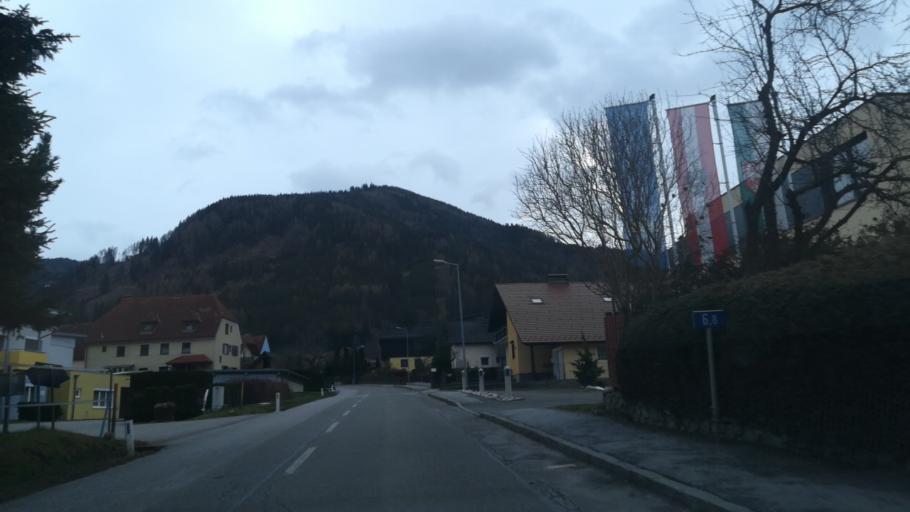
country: AT
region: Styria
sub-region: Politischer Bezirk Murtal
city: Sankt Georgen ob Judenburg
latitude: 47.2090
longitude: 14.4984
